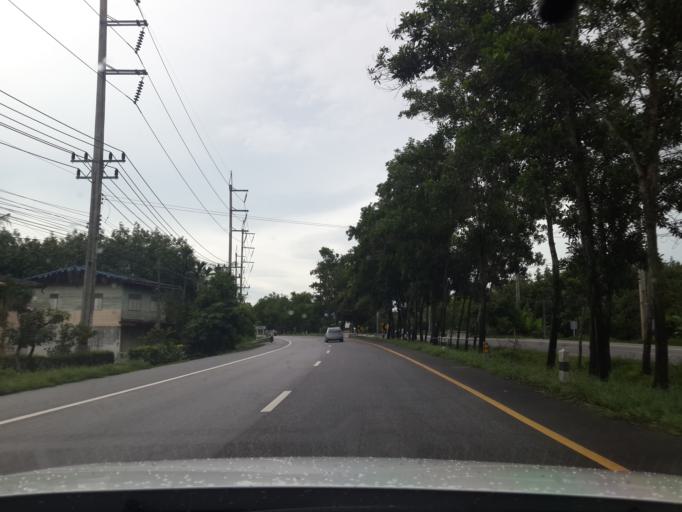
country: TH
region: Songkhla
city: Chana
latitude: 6.9567
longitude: 100.6894
